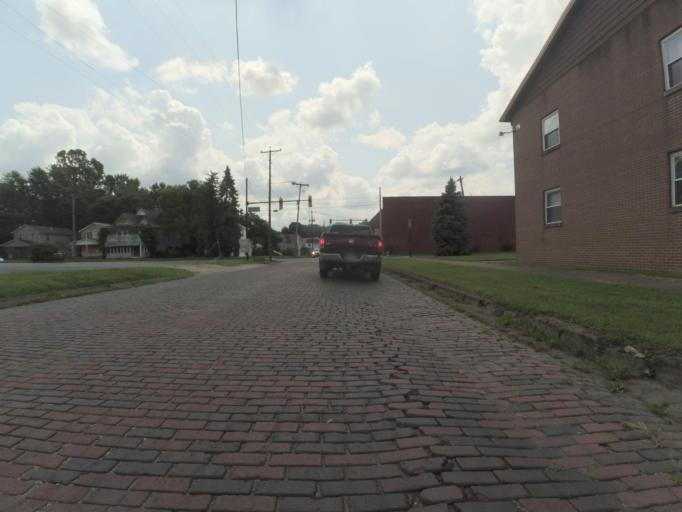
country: US
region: West Virginia
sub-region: Cabell County
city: Huntington
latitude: 38.4134
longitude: -82.4755
